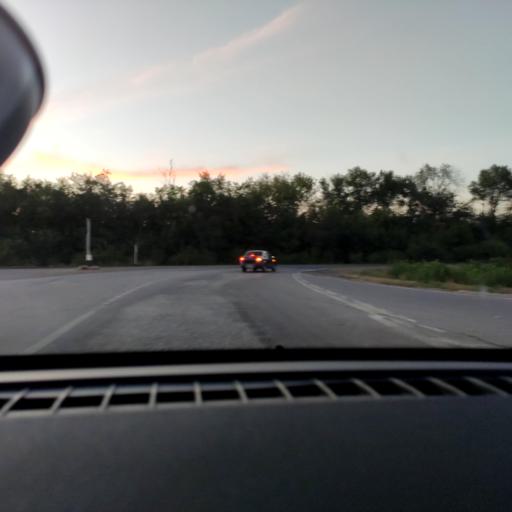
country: RU
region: Samara
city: Kinel'
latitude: 53.2658
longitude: 50.5435
